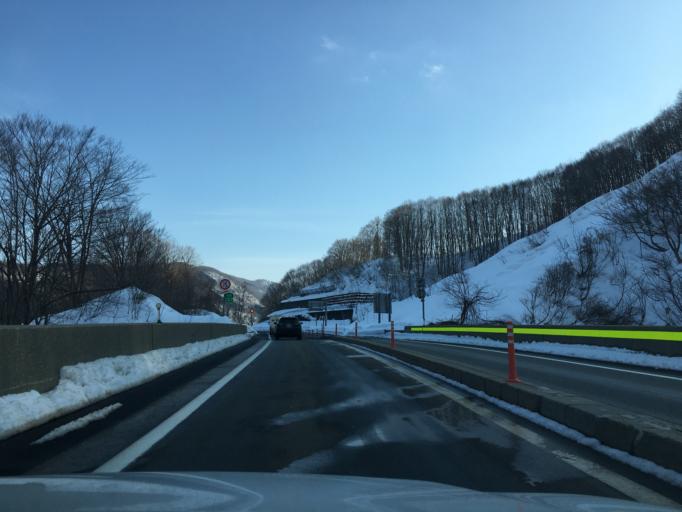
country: JP
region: Yamagata
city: Sagae
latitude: 38.4520
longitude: 139.9929
